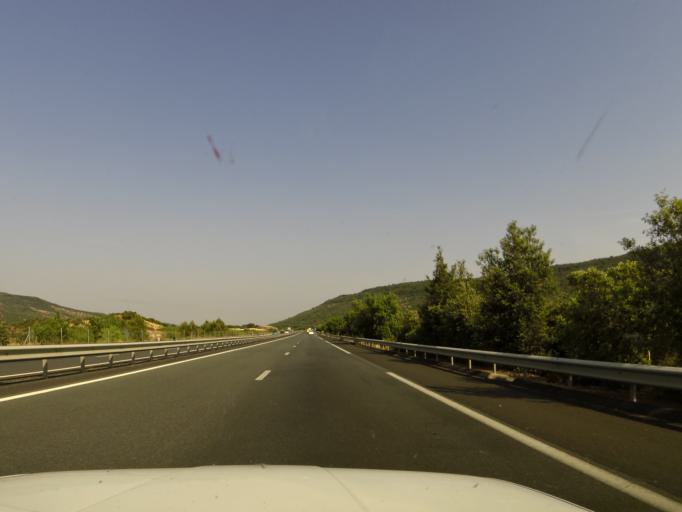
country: FR
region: Languedoc-Roussillon
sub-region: Departement de l'Herault
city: Lodeve
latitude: 43.6830
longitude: 3.3736
